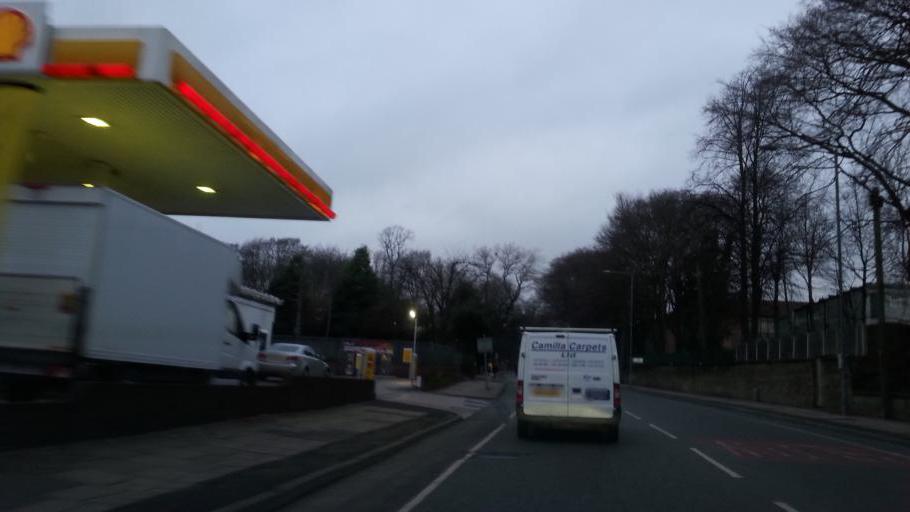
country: GB
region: England
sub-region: Borough of Bury
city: Prestwich
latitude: 53.5205
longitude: -2.2729
